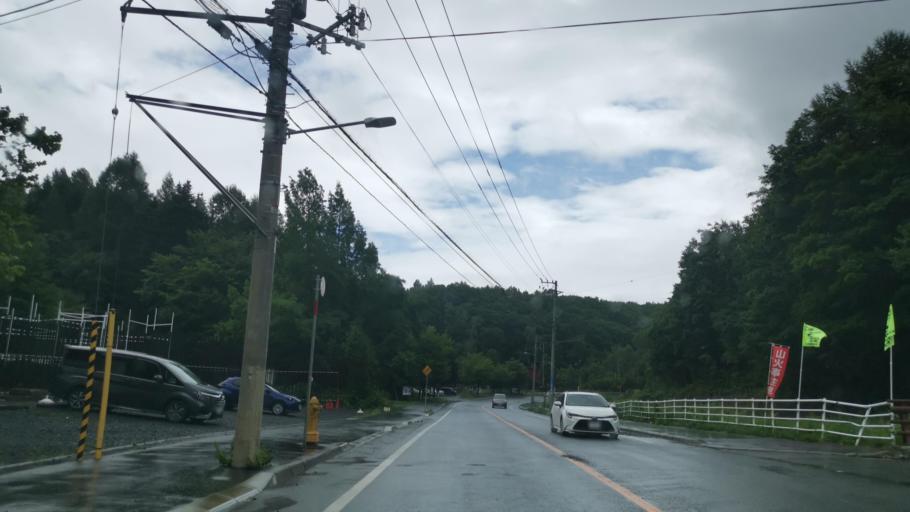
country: JP
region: Hokkaido
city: Sapporo
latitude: 42.9483
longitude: 141.3583
